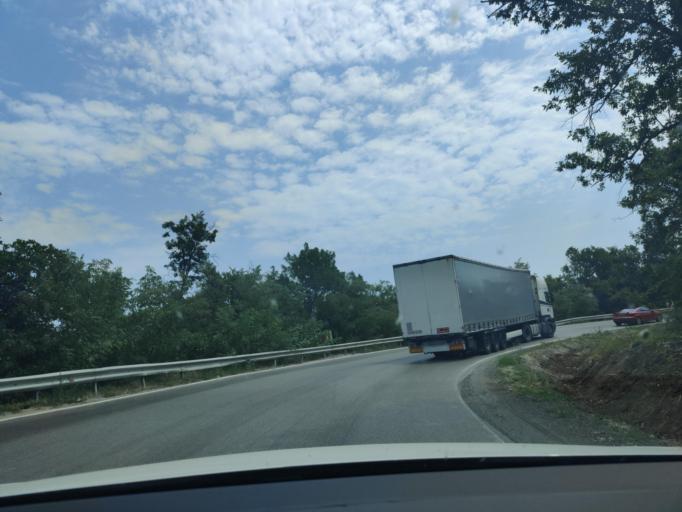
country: BG
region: Vidin
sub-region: Obshtina Dimovo
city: Dimovo
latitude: 43.6770
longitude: 22.7720
